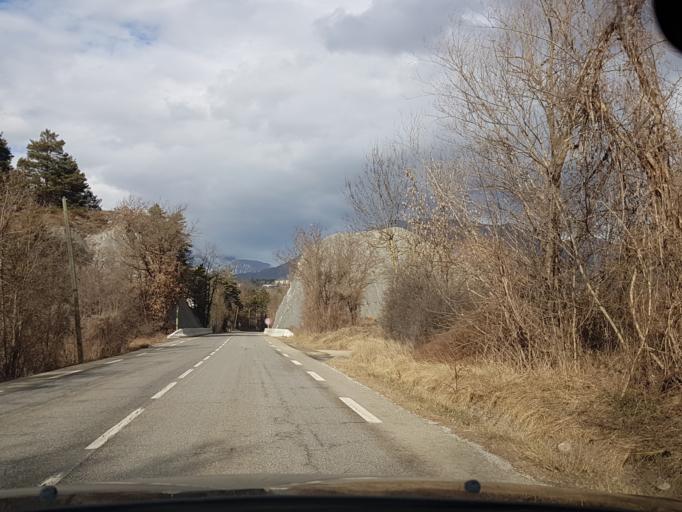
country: FR
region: Provence-Alpes-Cote d'Azur
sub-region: Departement des Hautes-Alpes
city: Gap
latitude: 44.5193
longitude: 6.0625
